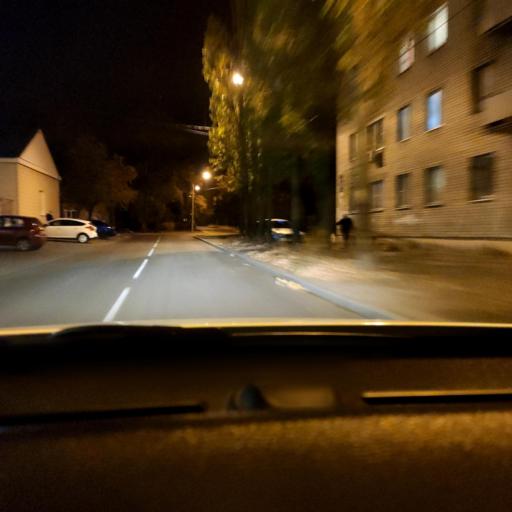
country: RU
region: Voronezj
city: Maslovka
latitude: 51.6165
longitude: 39.2451
